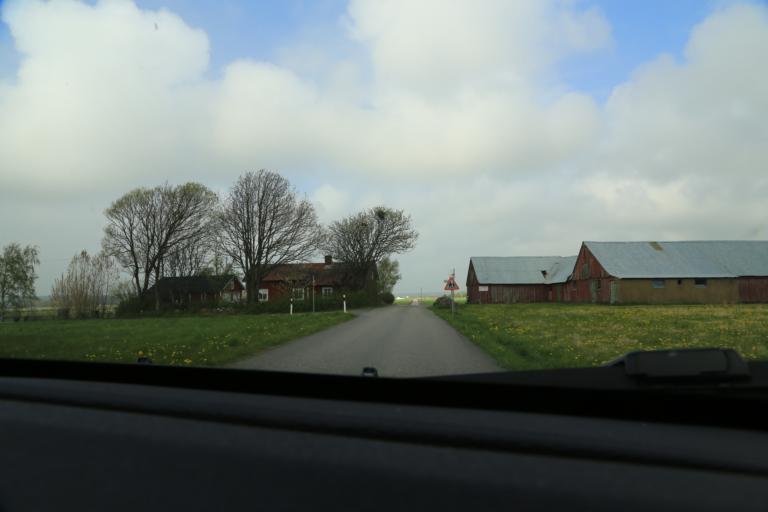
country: SE
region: Halland
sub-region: Kungsbacka Kommun
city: Frillesas
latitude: 57.2313
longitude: 12.1560
